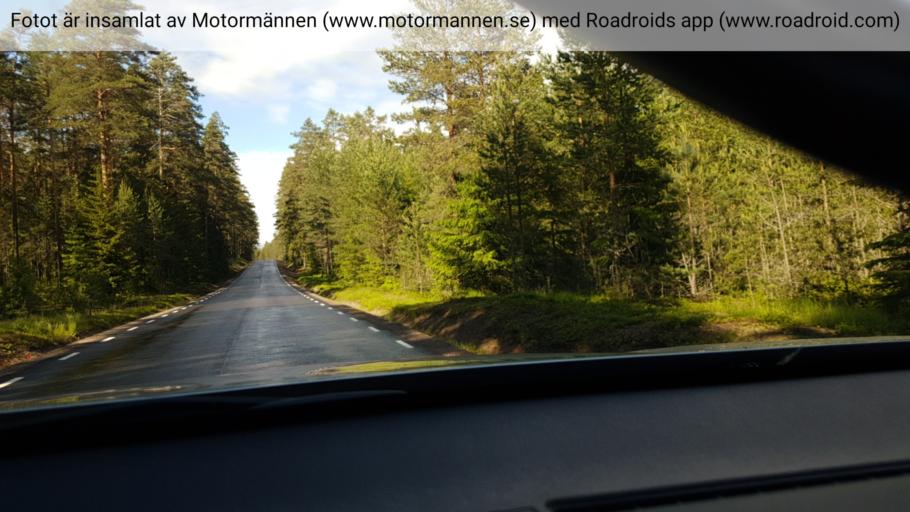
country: SE
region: Vaermland
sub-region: Hagfors Kommun
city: Ekshaerad
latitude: 60.2667
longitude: 13.4616
